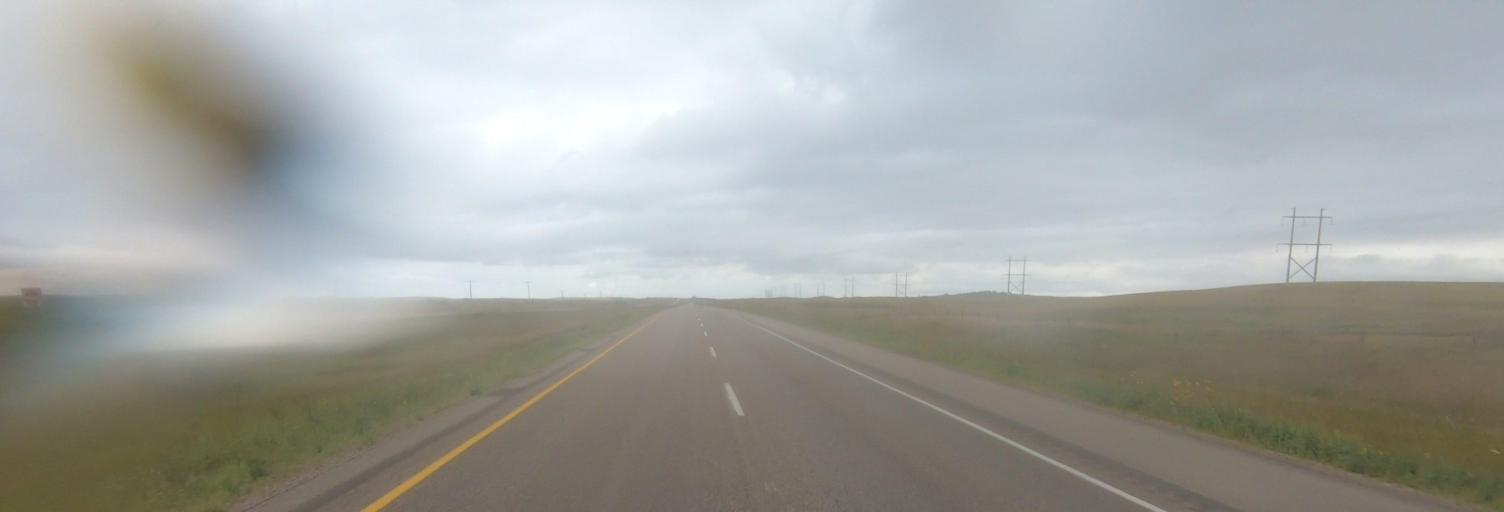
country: CA
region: Saskatchewan
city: Gravelbourg
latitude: 50.4630
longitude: -106.4051
